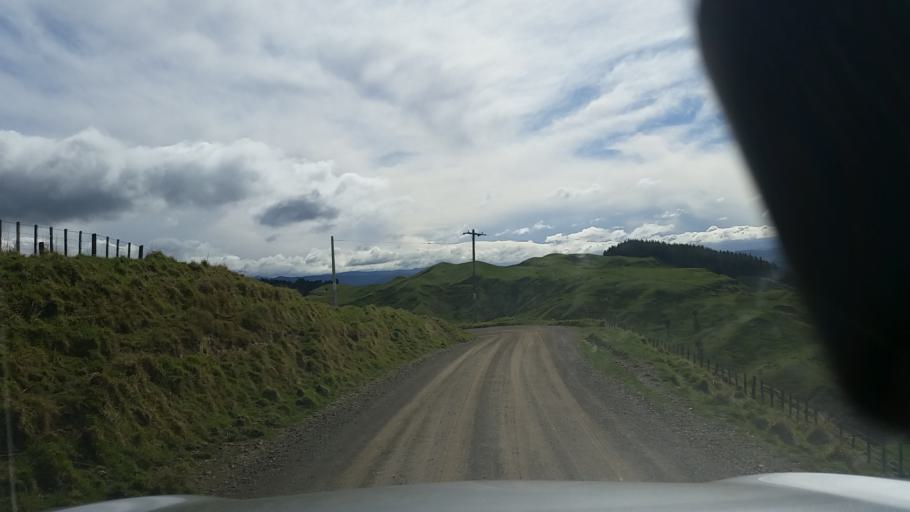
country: NZ
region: Hawke's Bay
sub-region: Napier City
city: Napier
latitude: -39.2095
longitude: 176.9581
